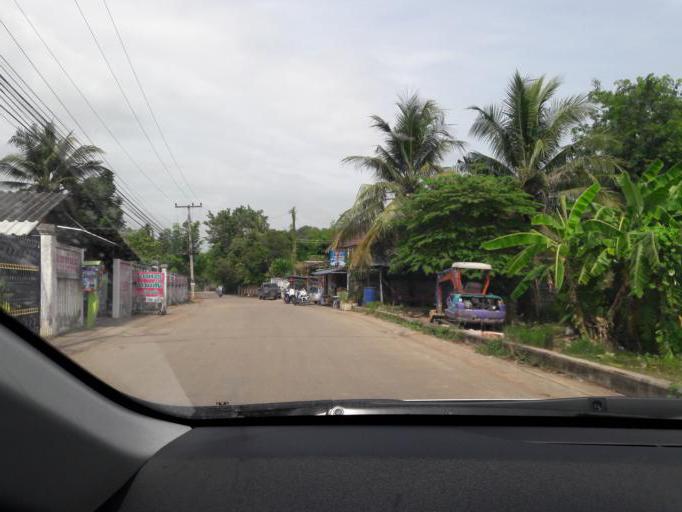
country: TH
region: Ratchaburi
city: Ratchaburi
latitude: 13.5205
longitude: 99.7934
